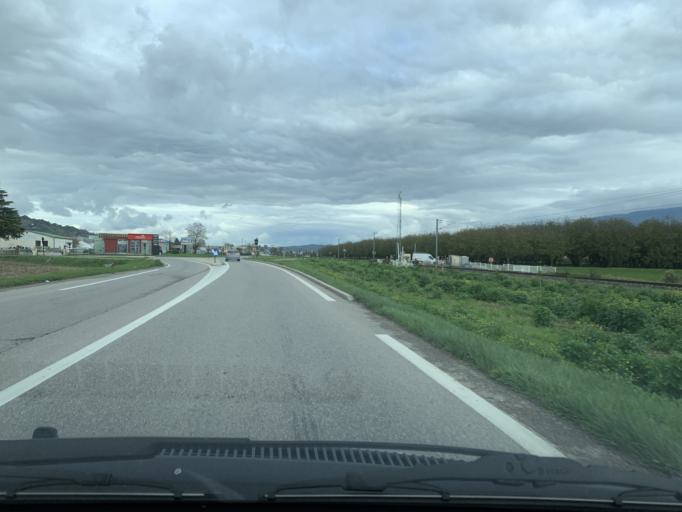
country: FR
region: Rhone-Alpes
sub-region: Departement de l'Isere
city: Chatte
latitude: 45.1339
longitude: 5.2933
